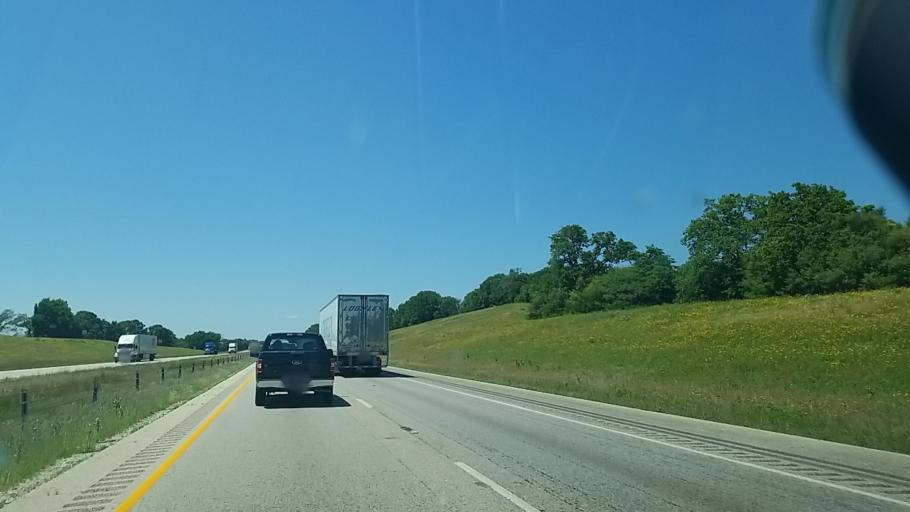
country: US
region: Texas
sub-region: Leon County
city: Buffalo
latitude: 31.4257
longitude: -96.0532
